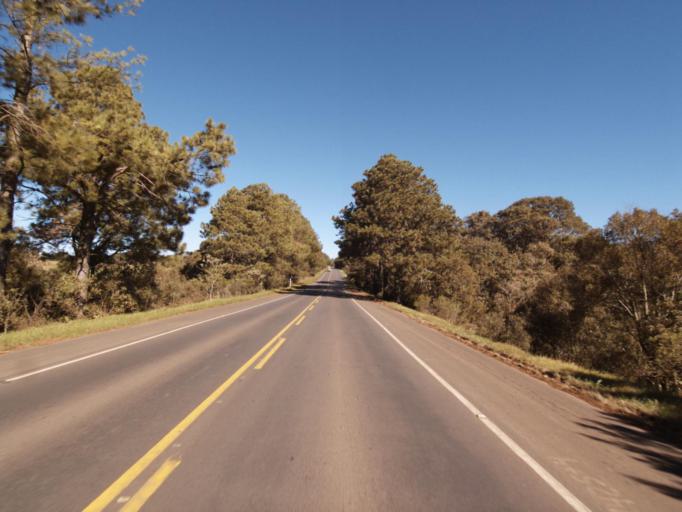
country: BR
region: Santa Catarina
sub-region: Joacaba
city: Joacaba
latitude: -26.9767
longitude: -51.7816
